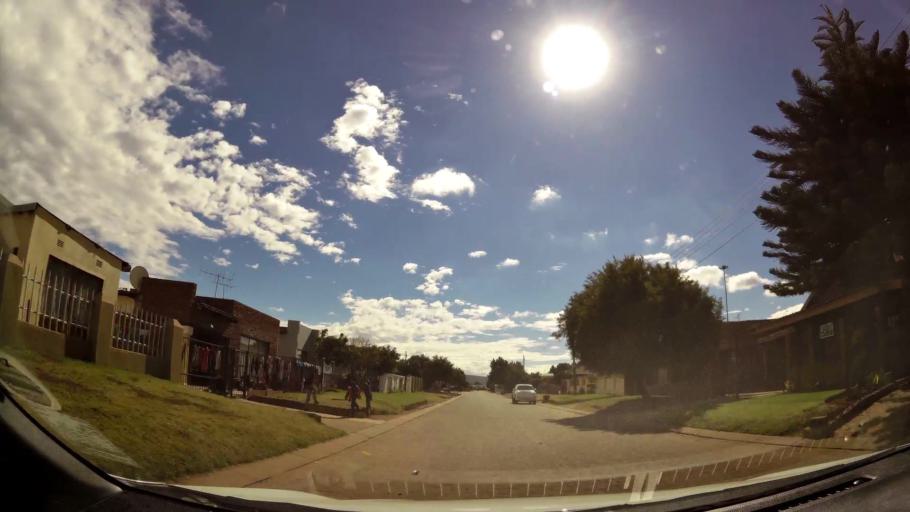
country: ZA
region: Limpopo
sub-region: Waterberg District Municipality
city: Bela-Bela
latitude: -24.8887
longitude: 28.3203
